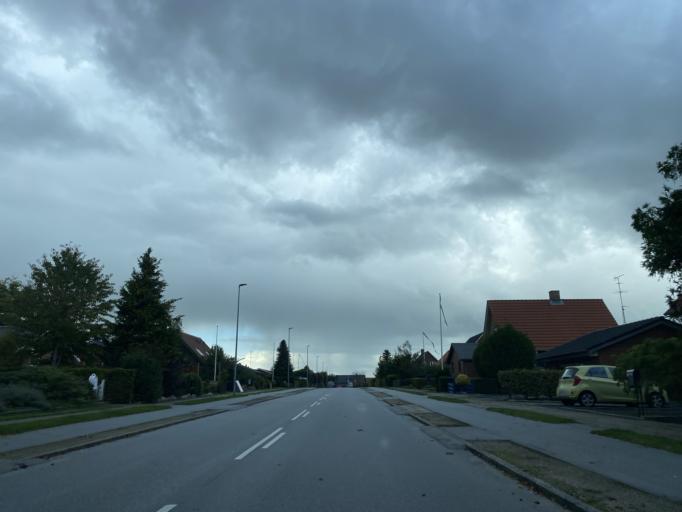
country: DK
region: South Denmark
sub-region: Haderslev Kommune
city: Haderslev
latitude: 55.2428
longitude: 9.4995
